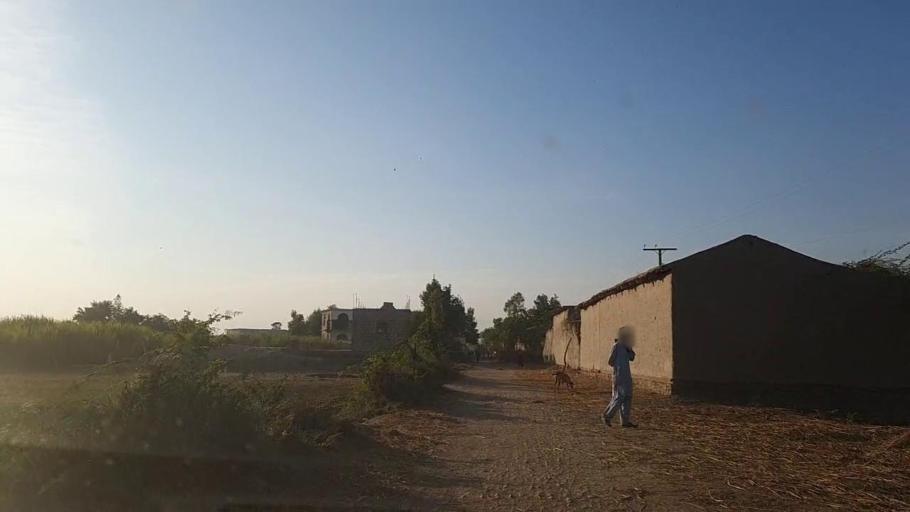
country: PK
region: Sindh
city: Mirpur Batoro
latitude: 24.6810
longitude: 68.2160
